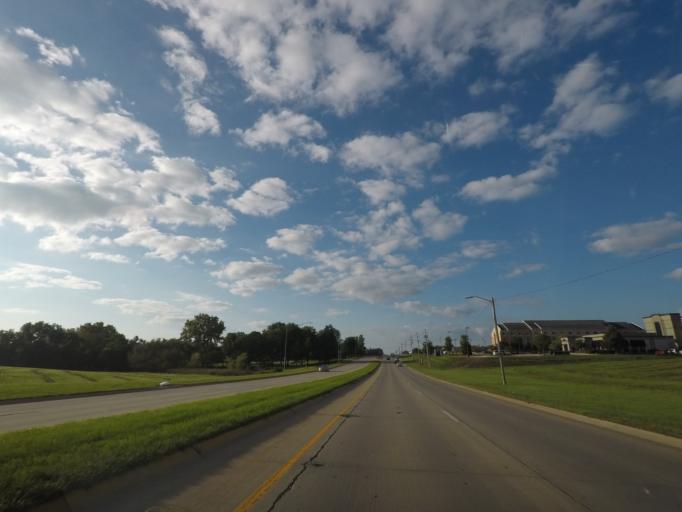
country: US
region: Iowa
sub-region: Warren County
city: Norwalk
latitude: 41.5239
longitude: -93.6450
